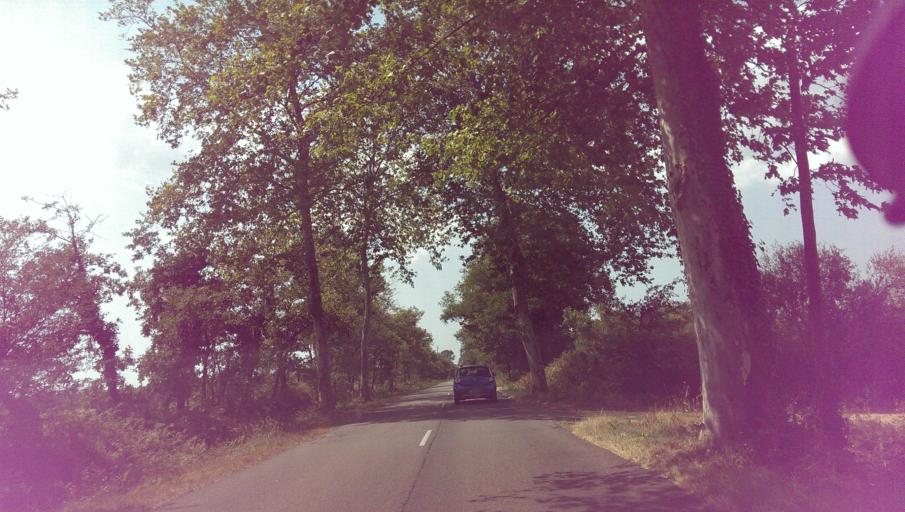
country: FR
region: Aquitaine
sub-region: Departement des Landes
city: Sabres
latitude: 44.1209
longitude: -0.6550
